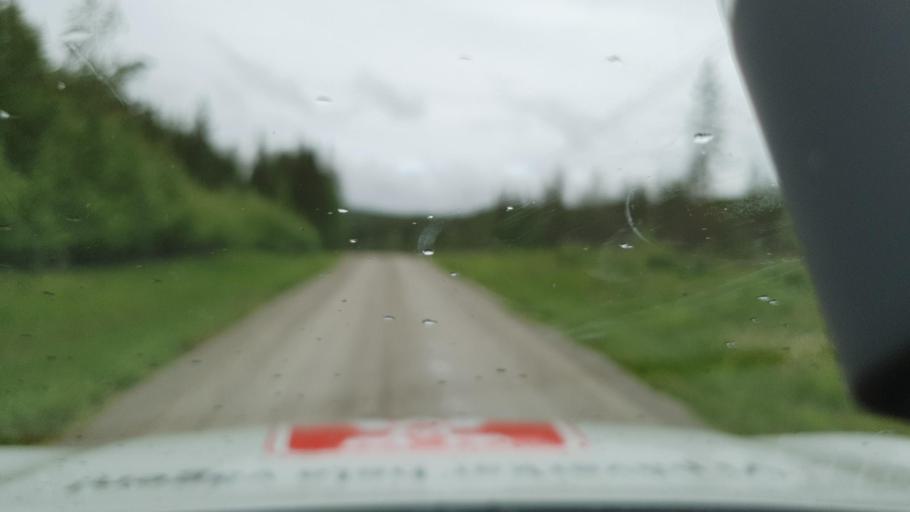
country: SE
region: Vaesterbotten
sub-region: Asele Kommun
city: Asele
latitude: 63.9686
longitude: 16.9290
